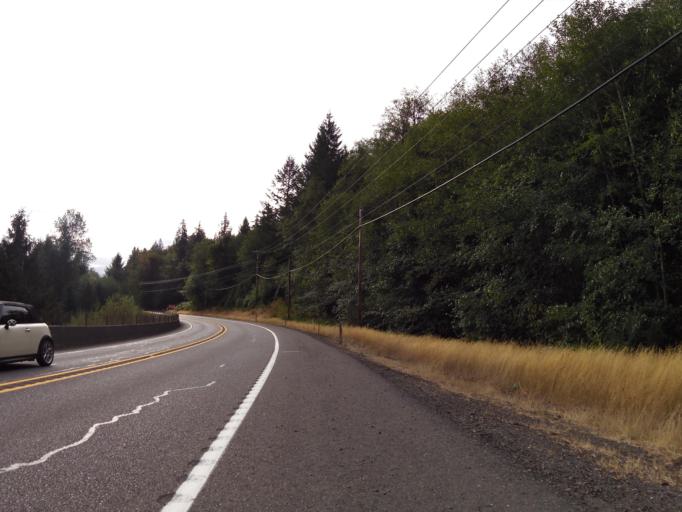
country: US
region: Washington
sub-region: Mason County
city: Allyn
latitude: 47.4026
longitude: -122.8376
